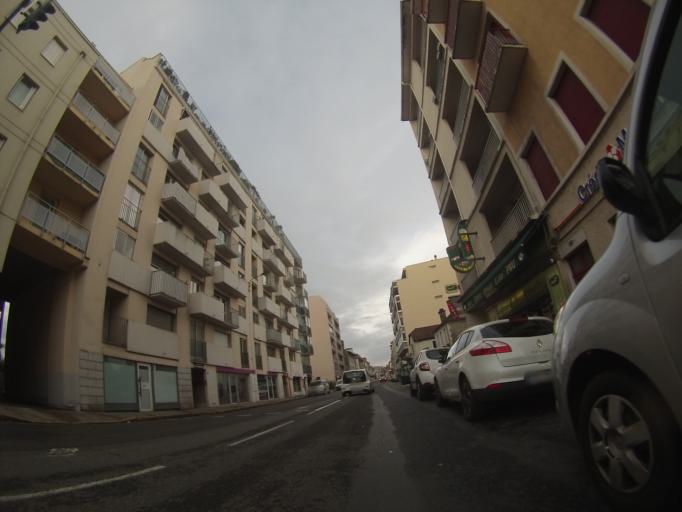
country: FR
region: Aquitaine
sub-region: Departement des Pyrenees-Atlantiques
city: Jurancon
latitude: 43.2873
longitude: -0.3804
